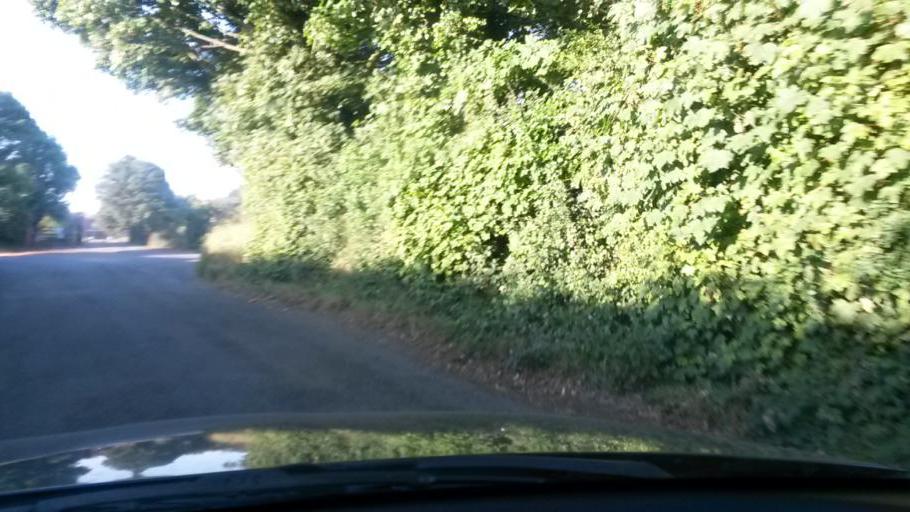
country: IE
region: Leinster
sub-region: Dublin City
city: Finglas
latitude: 53.4330
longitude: -6.3277
